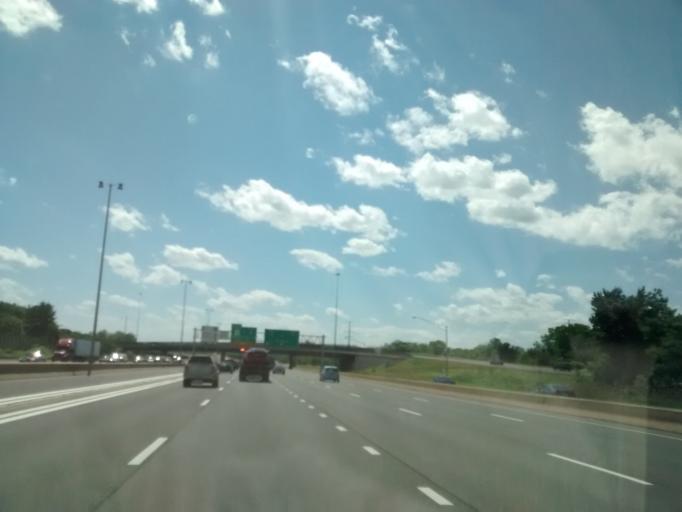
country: US
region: Connecticut
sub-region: Hartford County
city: East Hartford
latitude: 41.7665
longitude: -72.6228
